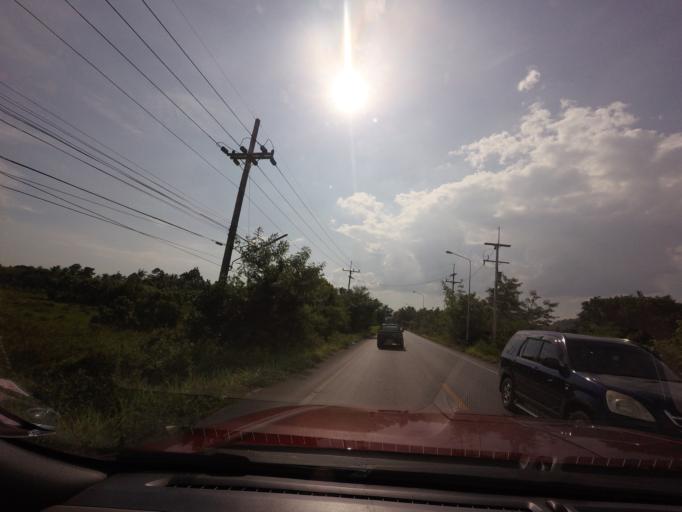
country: TH
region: Yala
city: Yala
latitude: 6.5554
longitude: 101.2249
